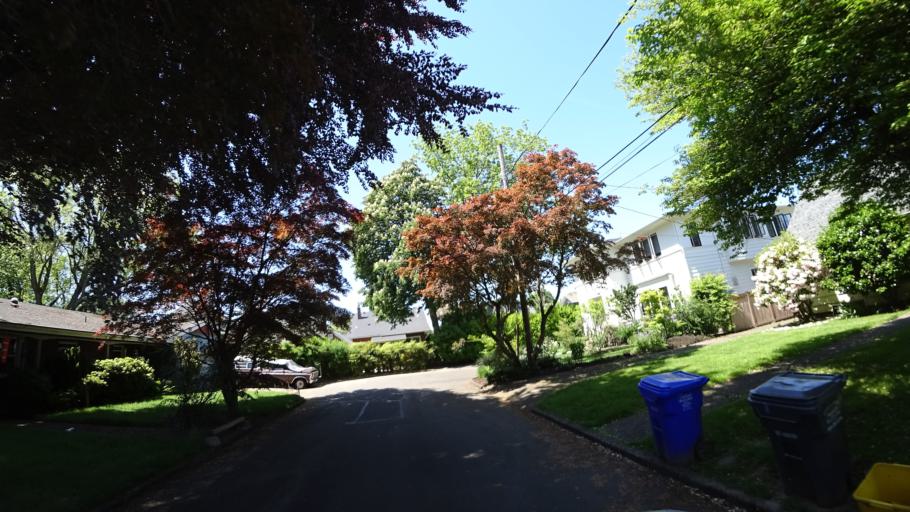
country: US
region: Oregon
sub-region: Multnomah County
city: Portland
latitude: 45.5412
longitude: -122.6372
